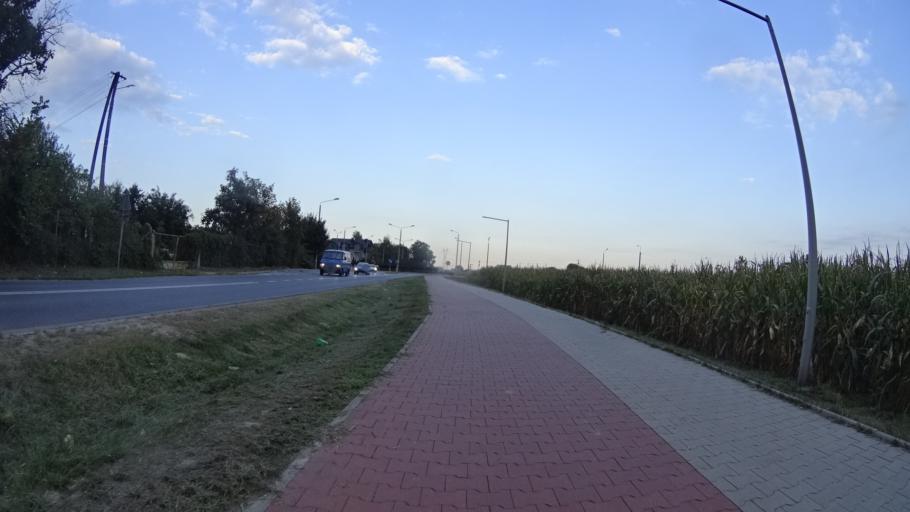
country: PL
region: Masovian Voivodeship
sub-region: Powiat warszawski zachodni
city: Ozarow Mazowiecki
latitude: 52.2314
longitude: 20.8147
